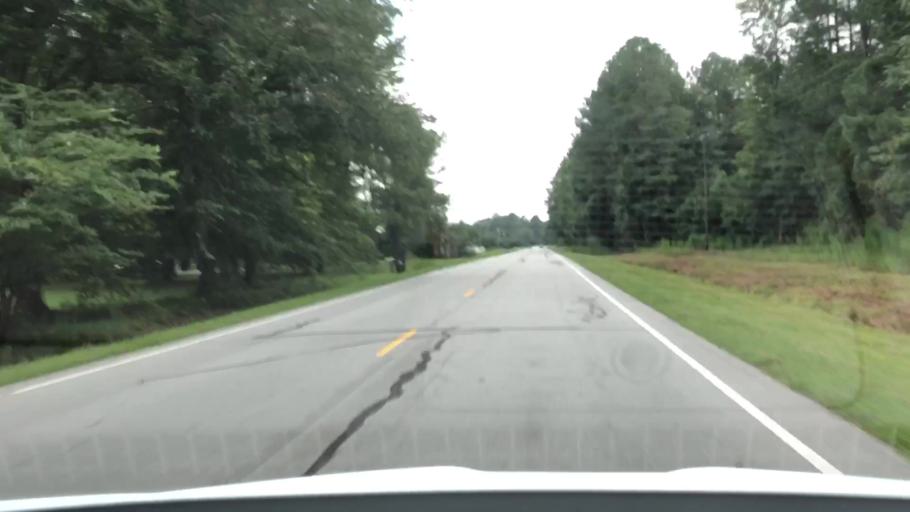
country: US
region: North Carolina
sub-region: Lenoir County
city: Kinston
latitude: 35.1162
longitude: -77.5122
